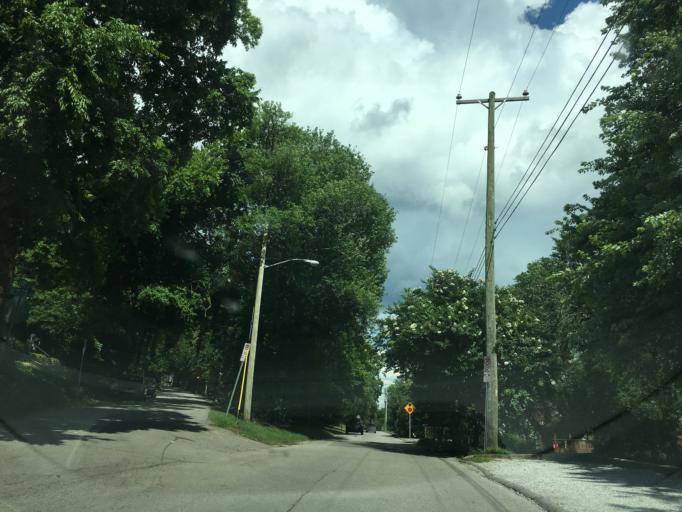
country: US
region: Tennessee
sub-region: Davidson County
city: Nashville
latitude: 36.1371
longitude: -86.8172
